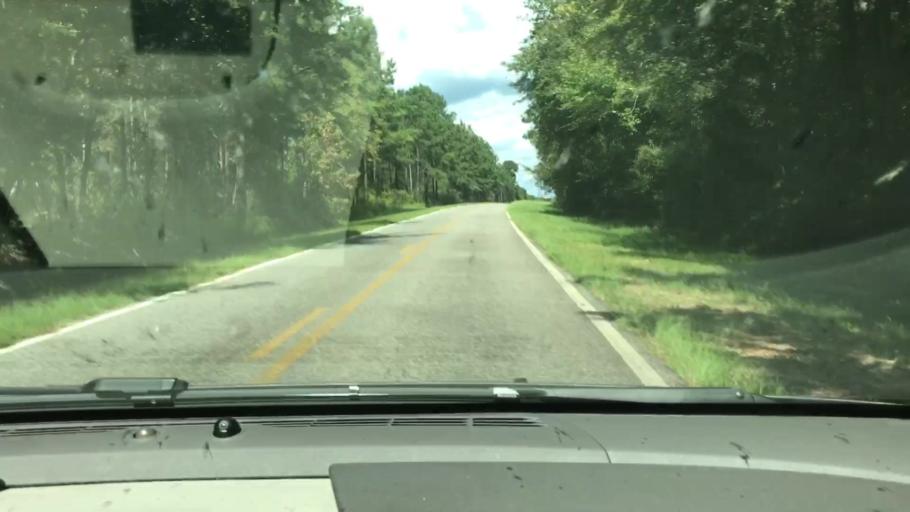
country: US
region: Georgia
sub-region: Clay County
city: Fort Gaines
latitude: 31.7353
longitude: -85.0913
